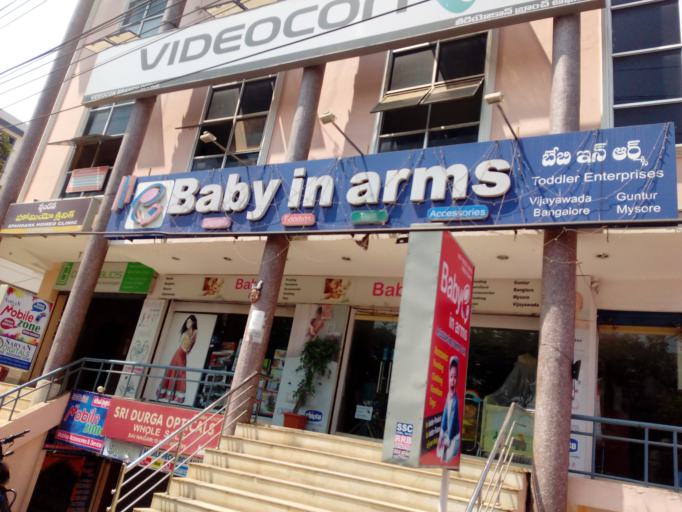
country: IN
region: Andhra Pradesh
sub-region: Krishna
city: Yanamalakuduru
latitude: 16.4997
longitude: 80.6555
